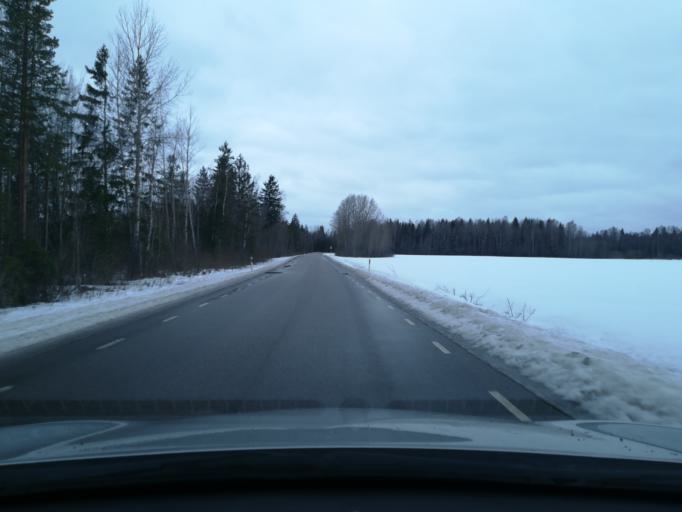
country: EE
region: Harju
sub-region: Nissi vald
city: Riisipere
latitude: 59.1334
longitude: 24.3009
